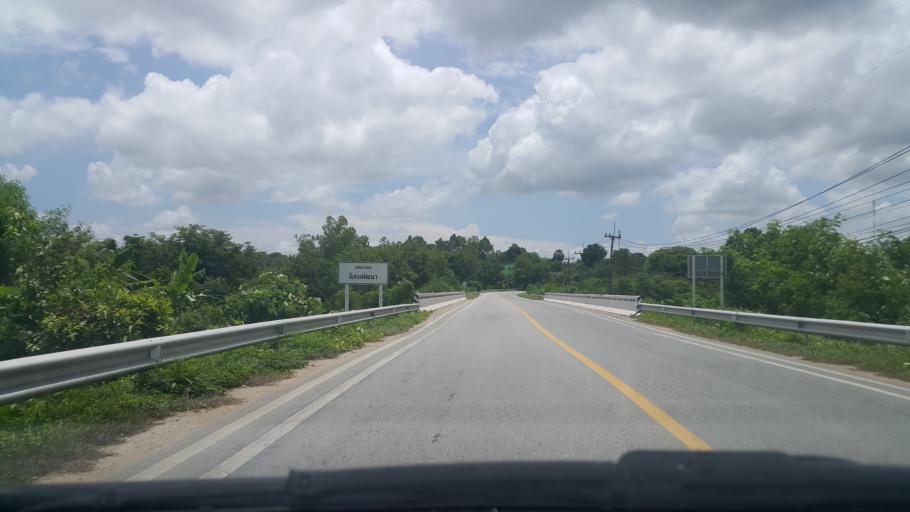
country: TH
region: Rayong
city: Ban Chang
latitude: 12.8194
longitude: 101.0597
